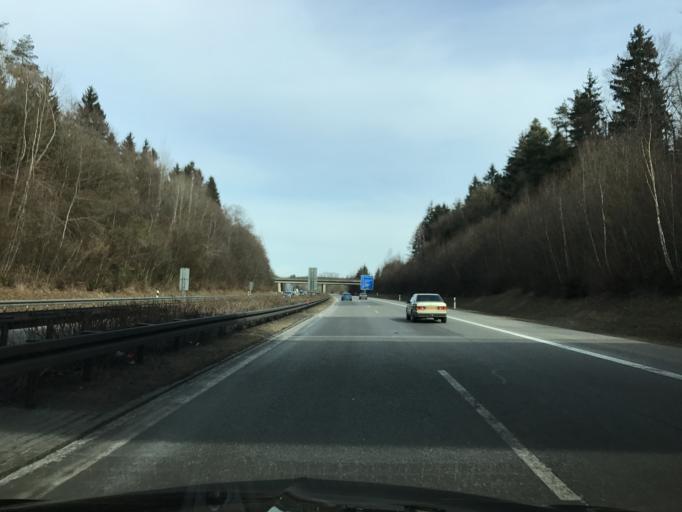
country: DE
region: Bavaria
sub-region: Swabia
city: Weissensberg
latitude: 47.5838
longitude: 9.7362
